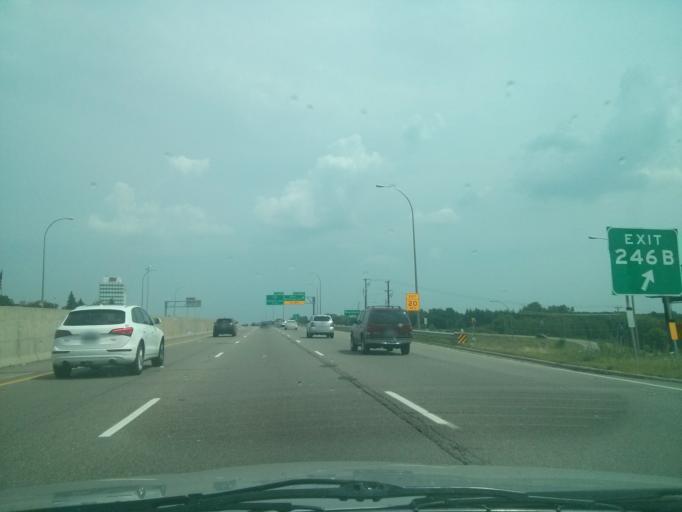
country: US
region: Minnesota
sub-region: Ramsey County
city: Maplewood
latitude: 44.9504
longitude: -93.0069
